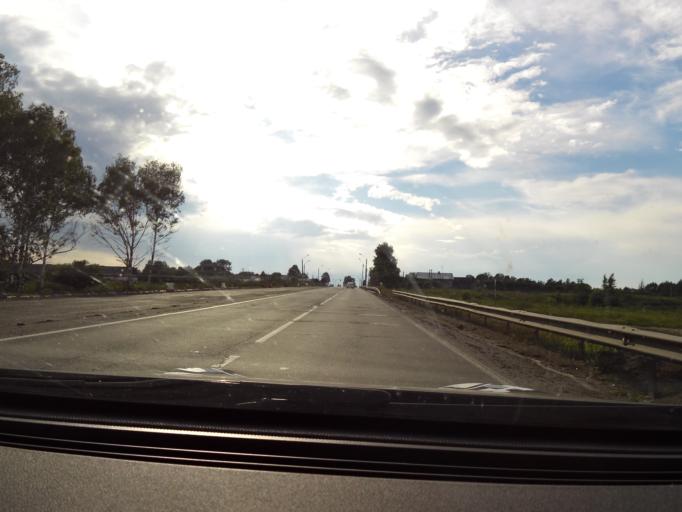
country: RU
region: Vladimir
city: Novovyazniki
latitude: 56.1716
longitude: 42.4275
